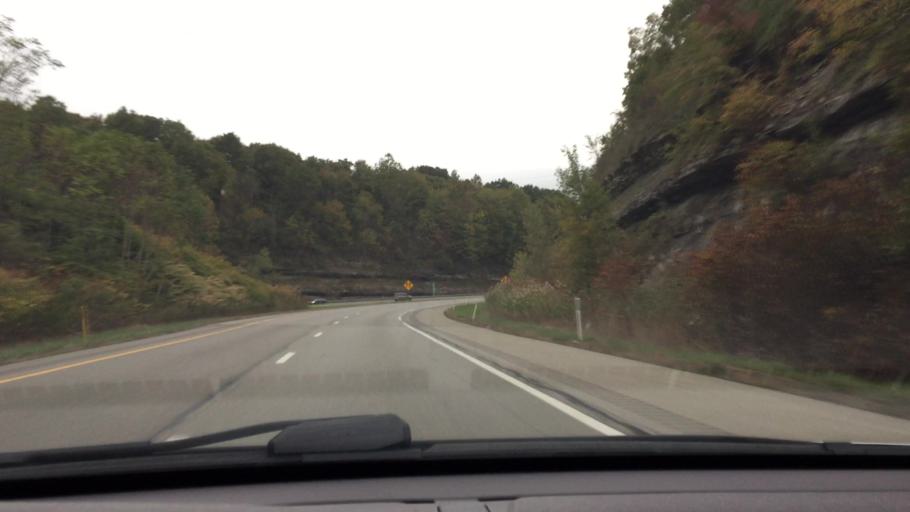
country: US
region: Pennsylvania
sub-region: Lawrence County
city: Oakwood
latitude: 40.9987
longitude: -80.3916
